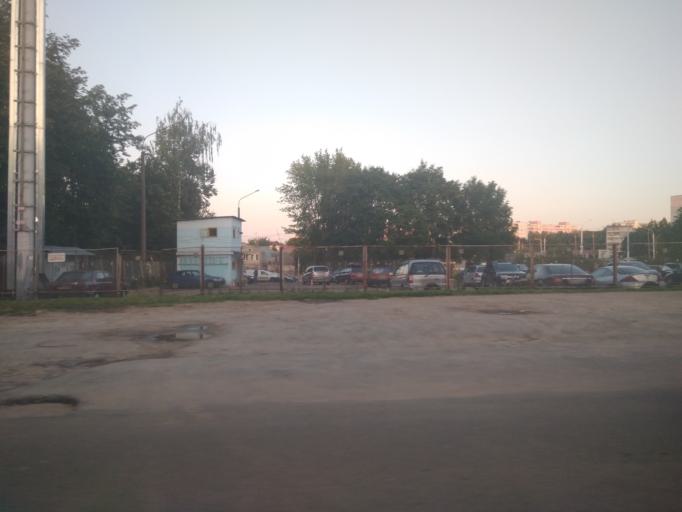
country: BY
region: Minsk
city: Novoye Medvezhino
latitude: 53.9261
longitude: 27.4757
